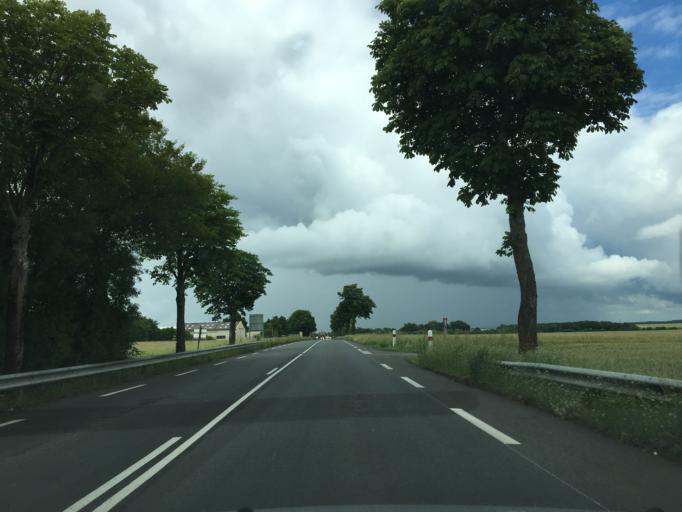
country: FR
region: Poitou-Charentes
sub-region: Departement des Deux-Sevres
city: Beauvoir-sur-Niort
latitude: 46.0819
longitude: -0.5055
